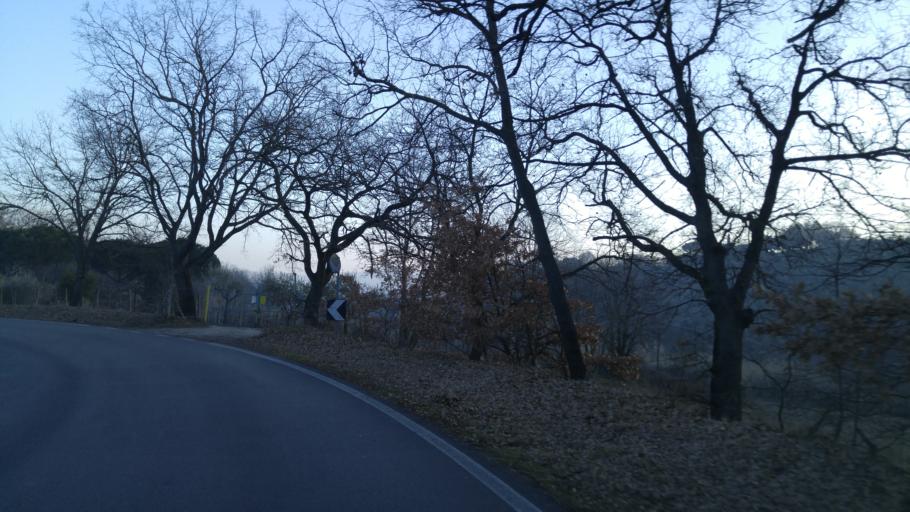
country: IT
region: The Marches
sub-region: Provincia di Pesaro e Urbino
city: Fenile
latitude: 43.8560
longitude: 12.9648
